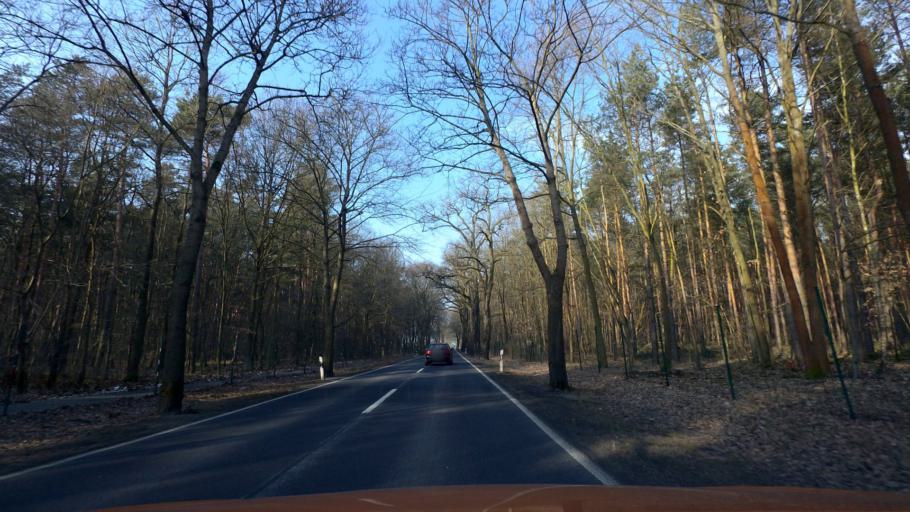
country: DE
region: Brandenburg
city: Ludwigsfelde
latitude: 52.2810
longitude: 13.2900
